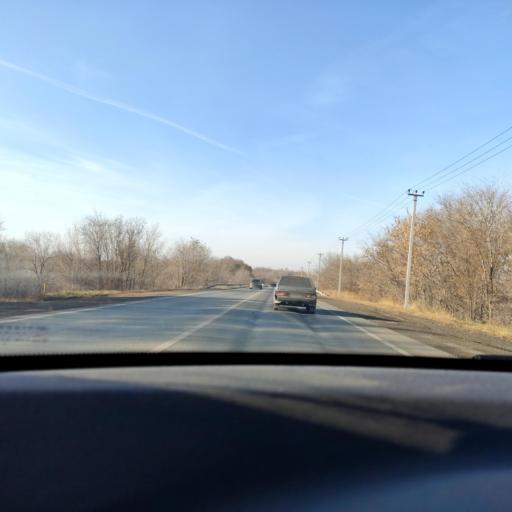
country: RU
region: Samara
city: Samara
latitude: 53.0812
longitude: 50.0865
